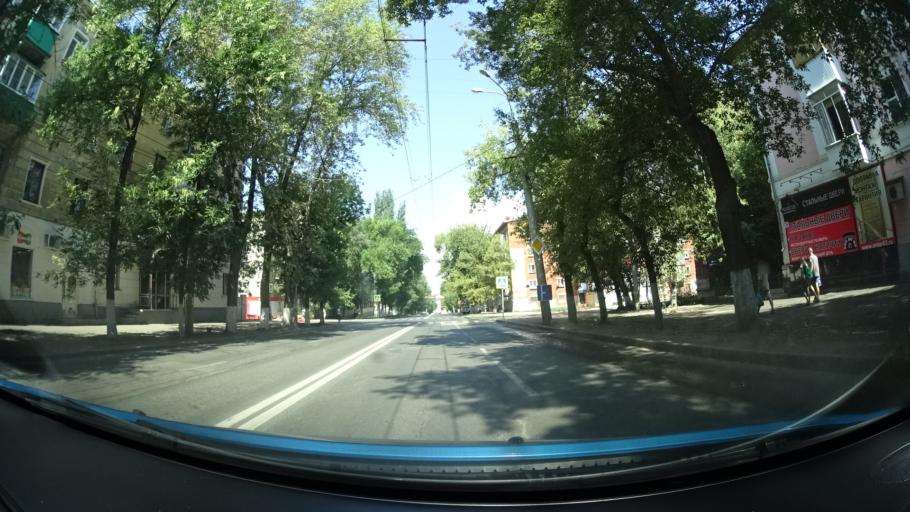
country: RU
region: Samara
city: Samara
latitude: 53.2125
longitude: 50.1541
